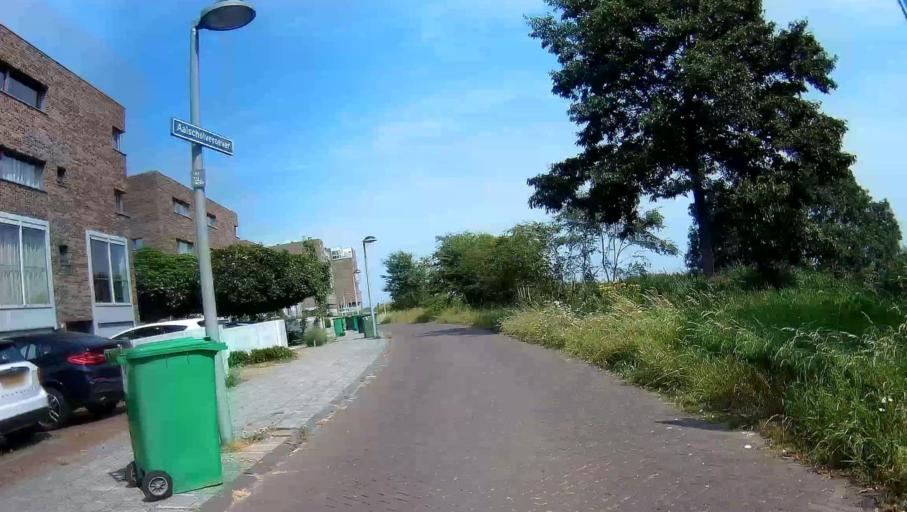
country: NL
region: South Holland
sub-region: Gemeente Pijnacker-Nootdorp
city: Pijnacker
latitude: 52.0617
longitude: 4.4200
